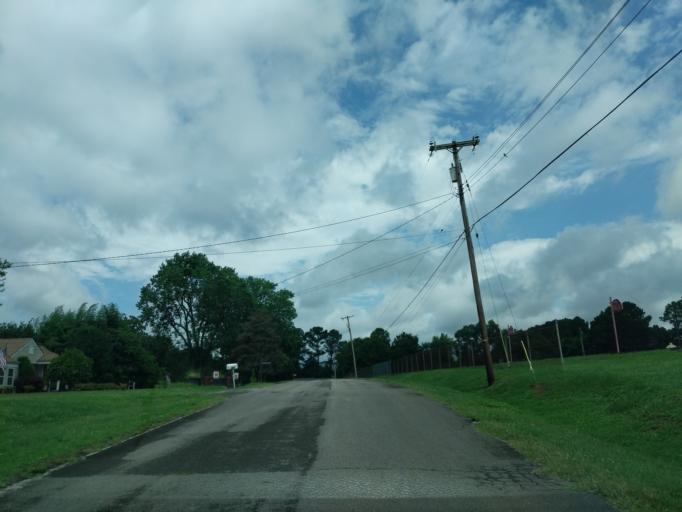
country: US
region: Tennessee
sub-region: Davidson County
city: Lakewood
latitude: 36.2376
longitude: -86.6740
